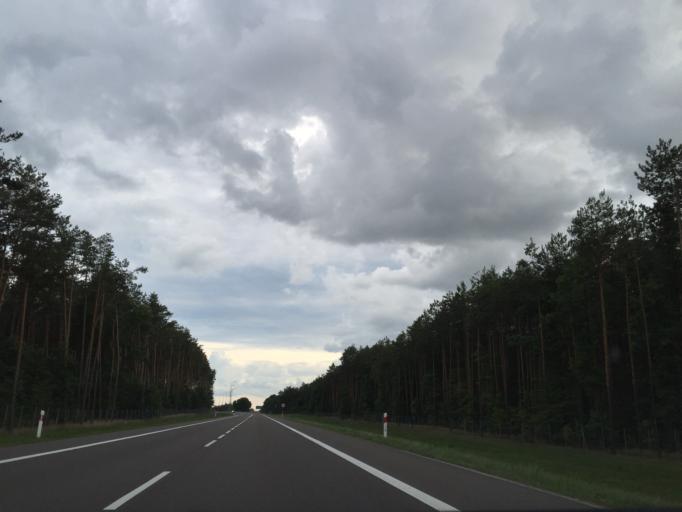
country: PL
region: Lublin Voivodeship
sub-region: Powiat lubartowski
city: Kock
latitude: 51.6651
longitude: 22.4700
